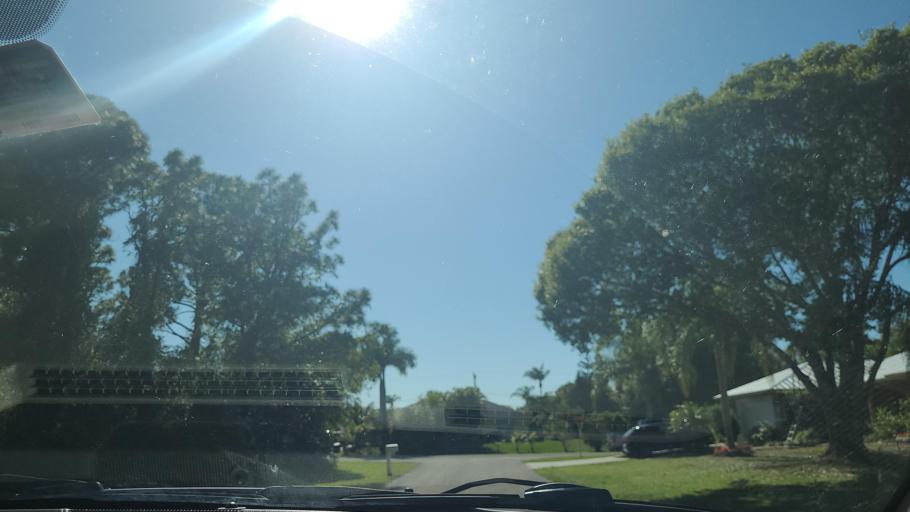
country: US
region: Florida
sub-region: Indian River County
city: Sebastian
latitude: 27.7682
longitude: -80.5004
